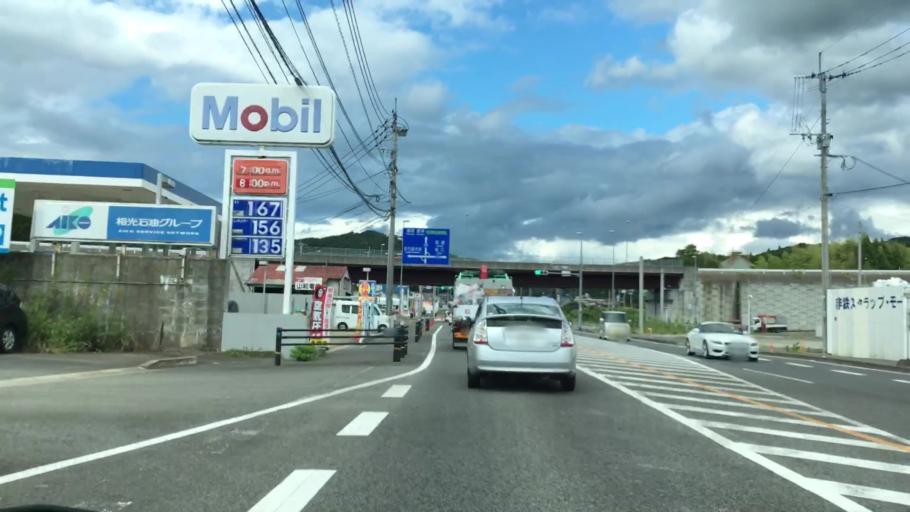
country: JP
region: Saga Prefecture
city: Imaricho-ko
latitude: 33.2807
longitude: 129.8960
